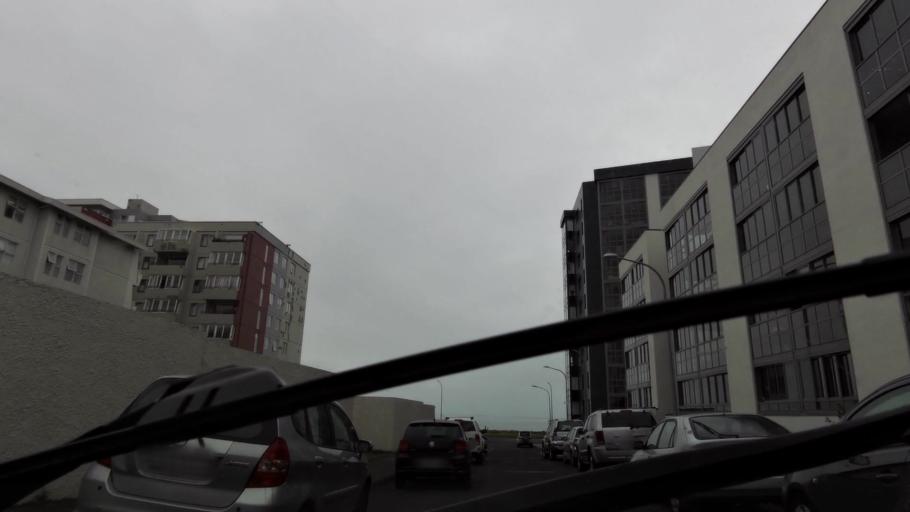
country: IS
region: Capital Region
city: Seltjarnarnes
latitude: 64.1500
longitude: -21.9629
